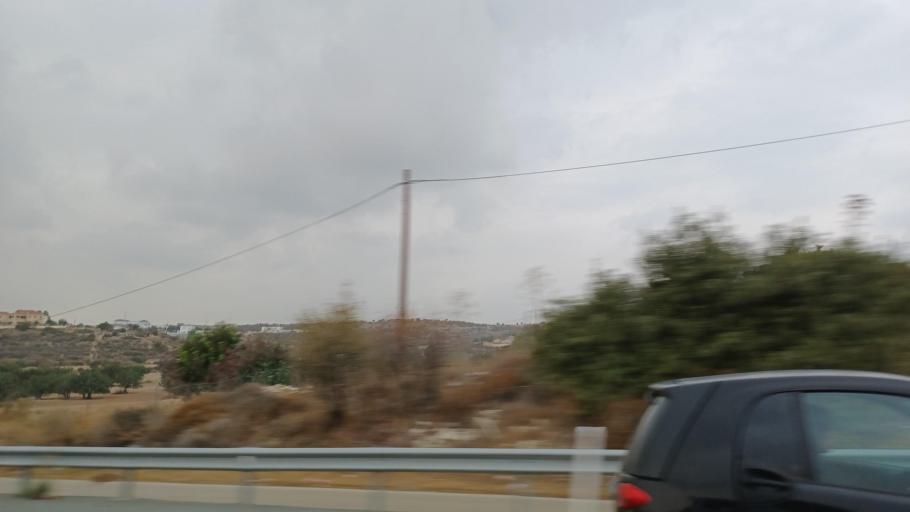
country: CY
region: Limassol
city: Erimi
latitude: 34.6908
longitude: 32.9281
